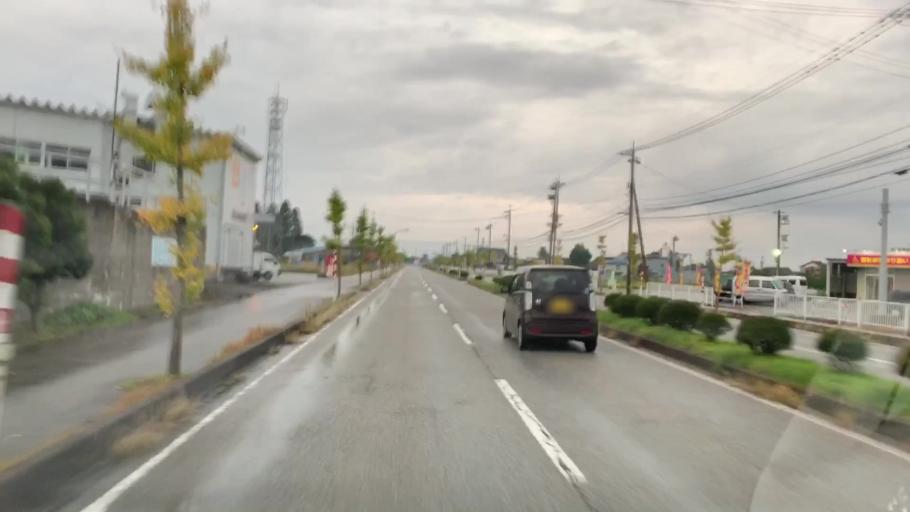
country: JP
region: Toyama
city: Kamiichi
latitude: 36.6897
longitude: 137.3393
